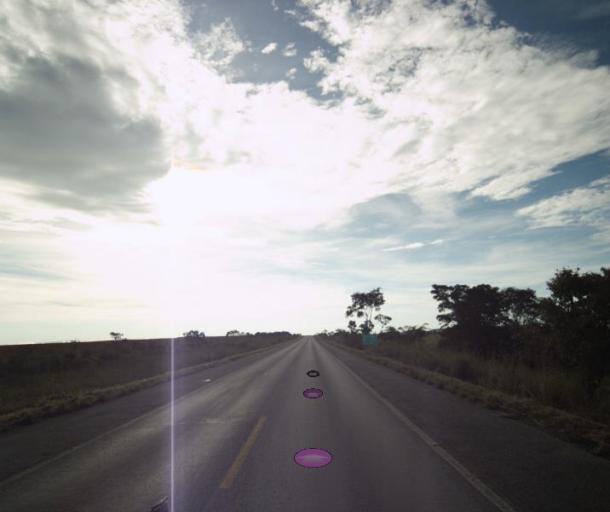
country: BR
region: Goias
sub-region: Pirenopolis
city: Pirenopolis
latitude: -15.7500
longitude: -48.6510
